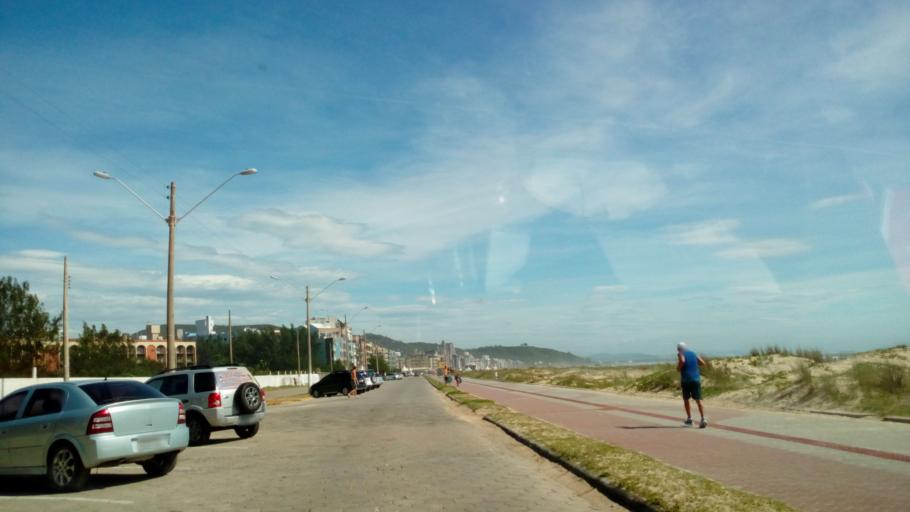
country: BR
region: Santa Catarina
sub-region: Laguna
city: Laguna
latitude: -28.4907
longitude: -48.7642
